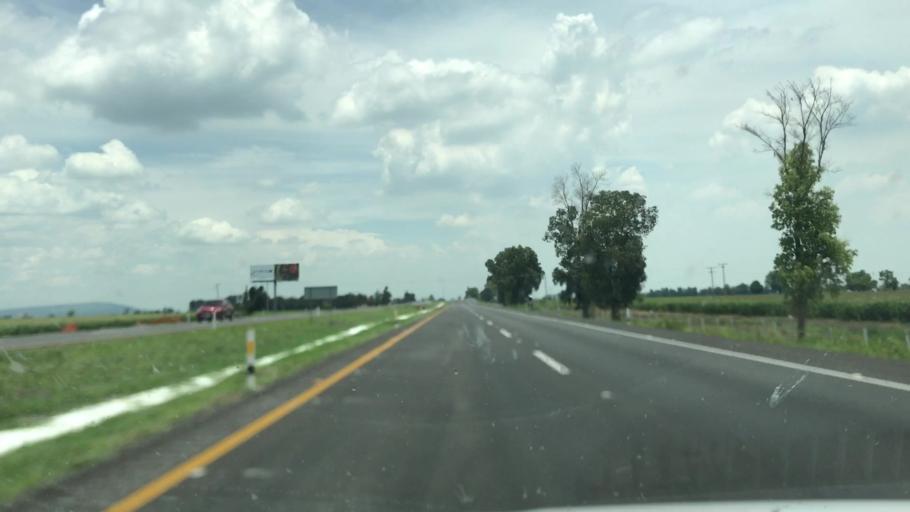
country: MX
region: Guanajuato
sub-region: Salamanca
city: San Vicente de Flores
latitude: 20.6332
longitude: -101.2543
